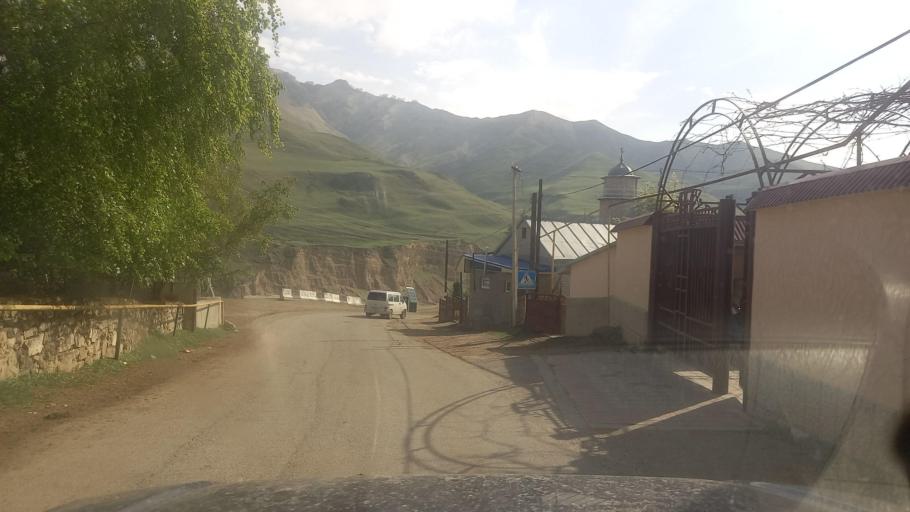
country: RU
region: Kabardino-Balkariya
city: Kamennomostskoye
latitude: 43.7264
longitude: 42.9232
